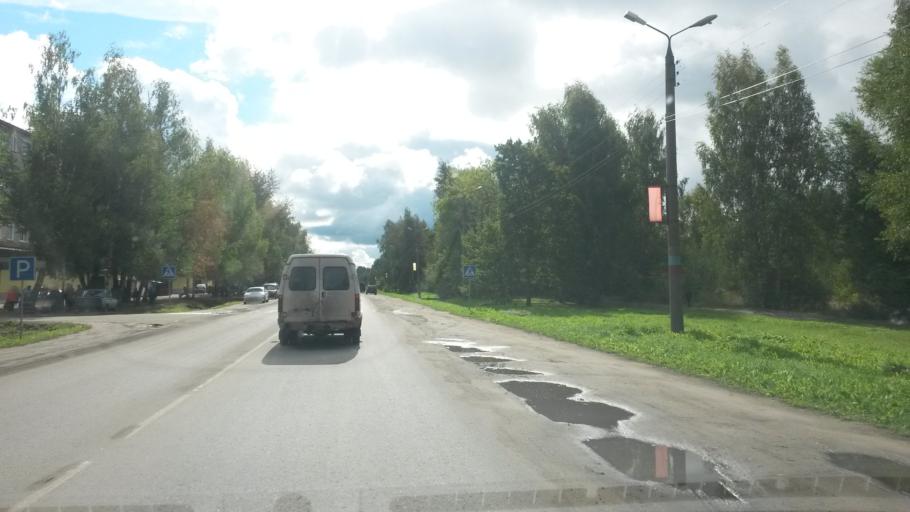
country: RU
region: Ivanovo
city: Zavolzhsk
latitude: 57.4860
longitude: 42.1433
